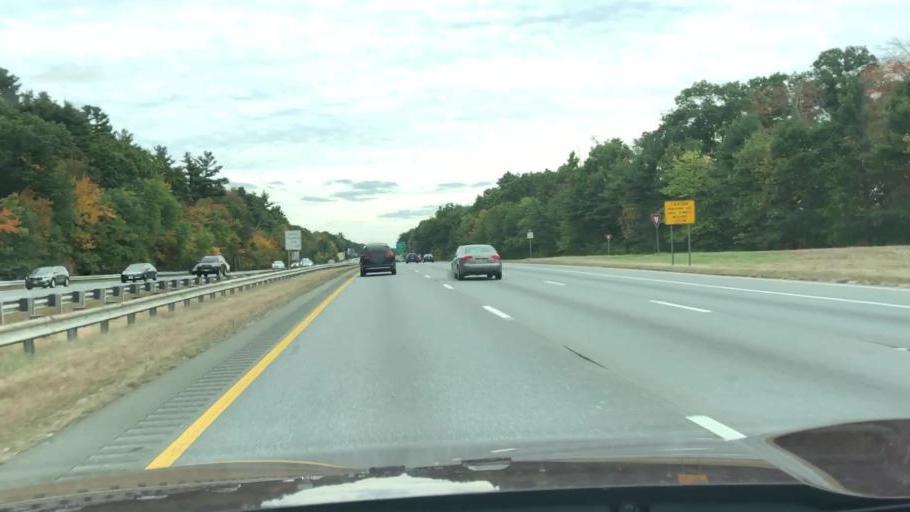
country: US
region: Massachusetts
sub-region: Essex County
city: Andover
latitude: 42.6430
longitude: -71.1847
